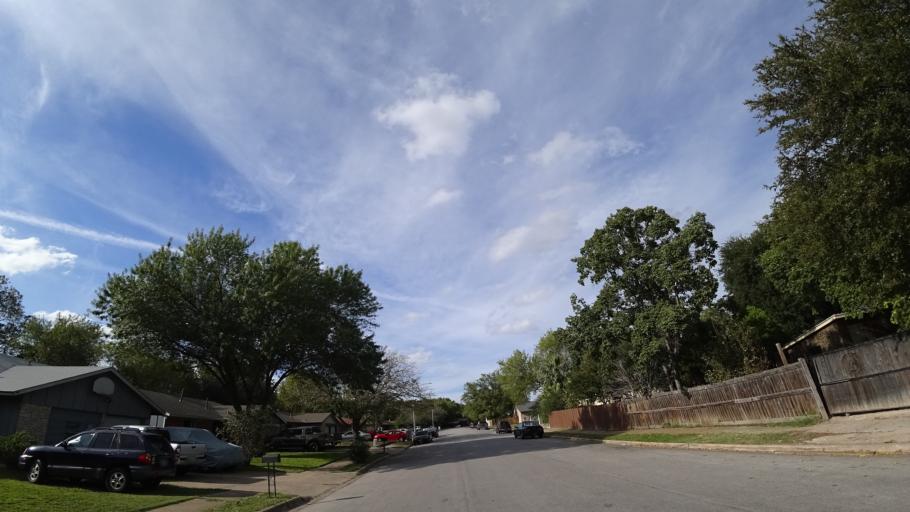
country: US
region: Texas
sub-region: Travis County
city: Onion Creek
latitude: 30.1945
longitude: -97.7527
